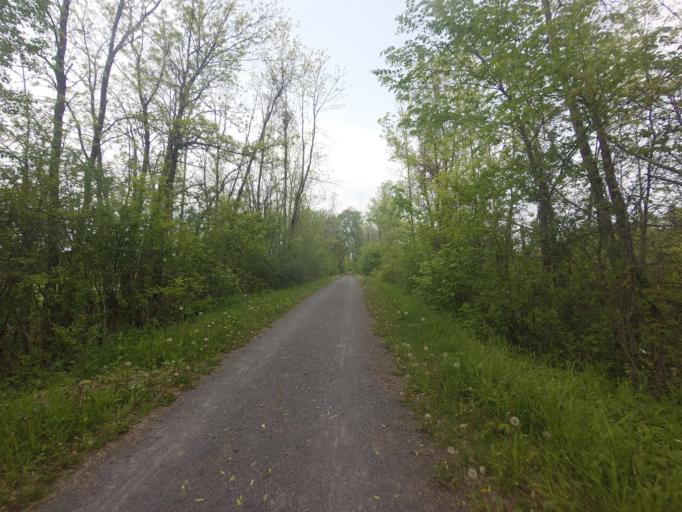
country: CA
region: Ontario
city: Kingston
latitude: 44.2920
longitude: -76.5586
